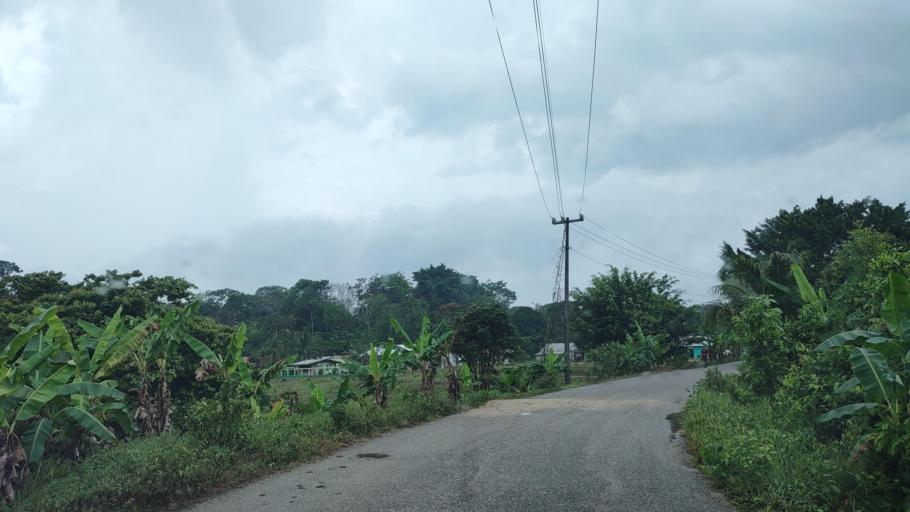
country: MX
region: Veracruz
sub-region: Uxpanapa
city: Poblado 10
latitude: 17.4712
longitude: -94.1206
